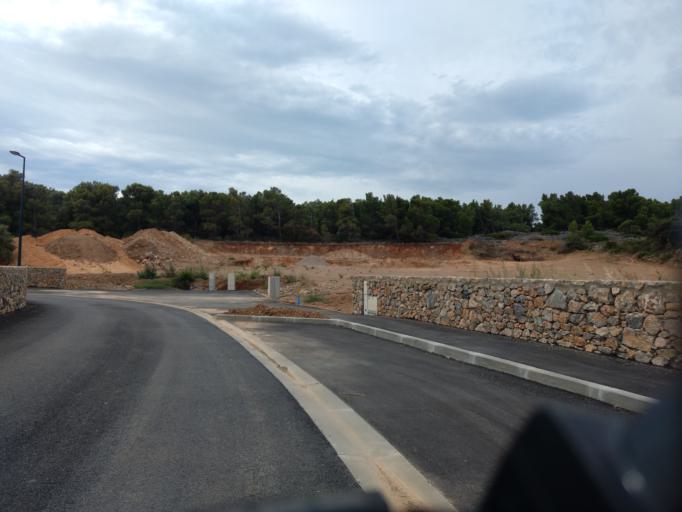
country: FR
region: Languedoc-Roussillon
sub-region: Departement de l'Aude
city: Leucate
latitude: 42.9032
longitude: 3.0272
